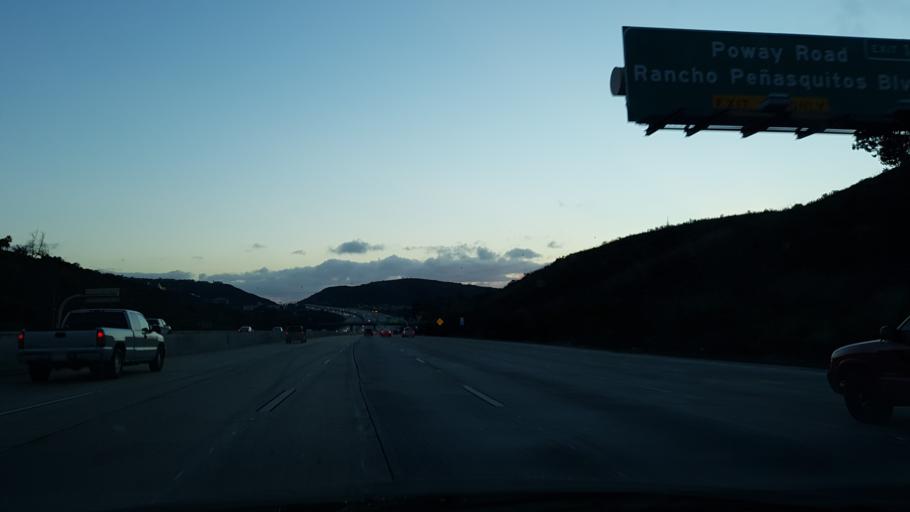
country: US
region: California
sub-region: San Diego County
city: Poway
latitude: 32.9546
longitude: -117.1020
